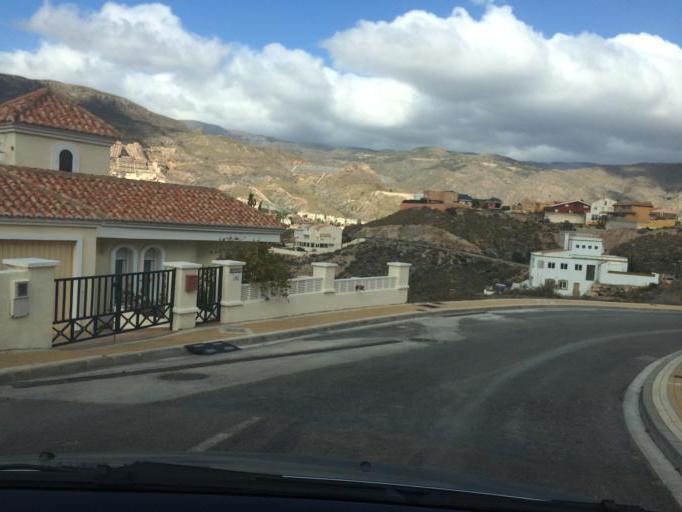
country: ES
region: Andalusia
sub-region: Provincia de Almeria
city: Vicar
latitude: 36.8305
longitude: -2.6128
